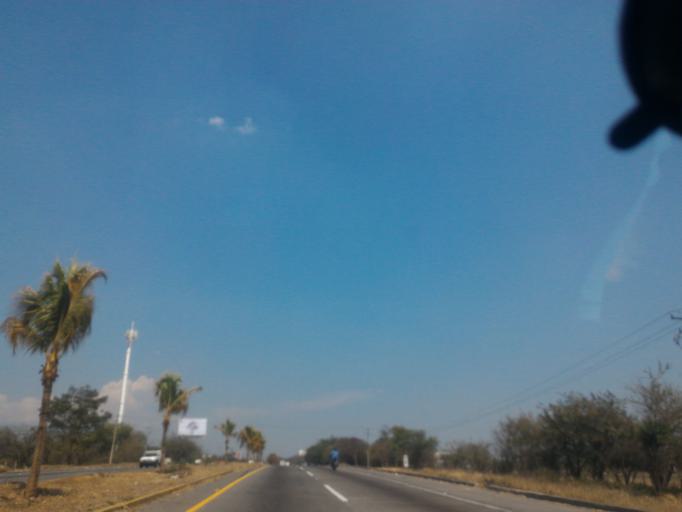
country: MX
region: Colima
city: Colima
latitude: 19.2178
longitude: -103.7158
